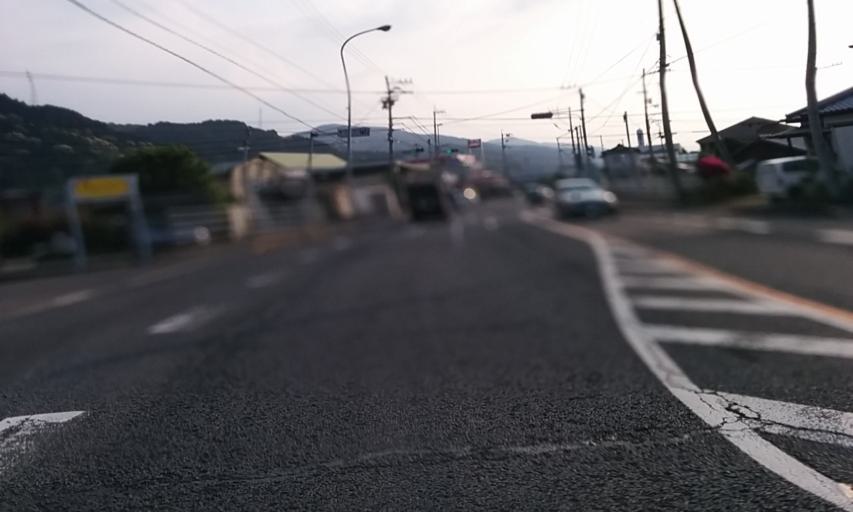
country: JP
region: Ehime
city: Saijo
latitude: 33.9003
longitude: 133.1814
